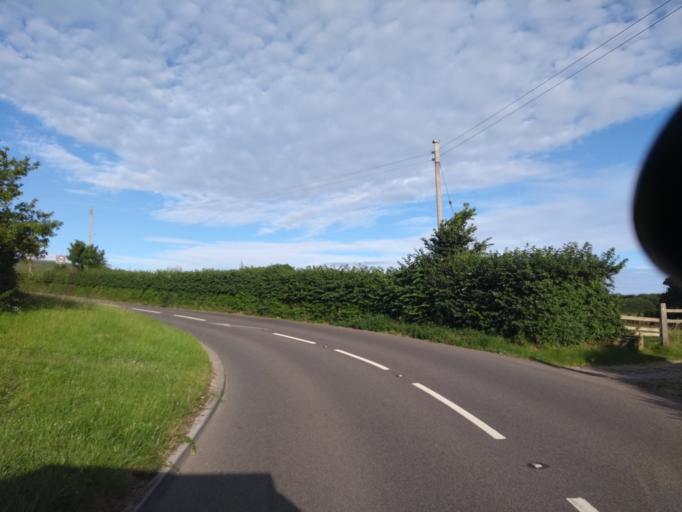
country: GB
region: England
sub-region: Somerset
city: Williton
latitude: 51.1792
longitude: -3.2233
